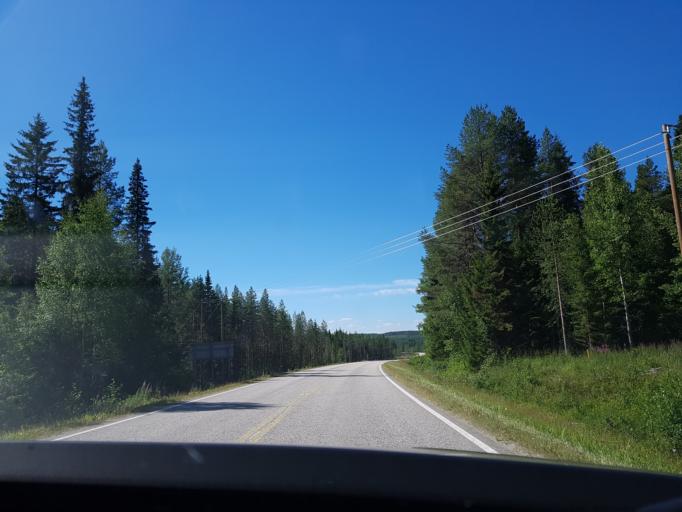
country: FI
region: Kainuu
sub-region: Kehys-Kainuu
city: Kuhmo
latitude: 64.1688
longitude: 29.6549
